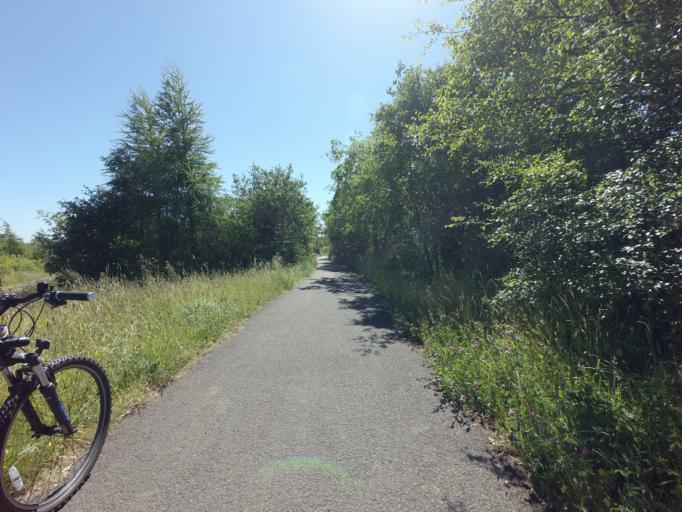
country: GB
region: Scotland
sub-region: West Lothian
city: West Calder
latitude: 55.8837
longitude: -3.5869
